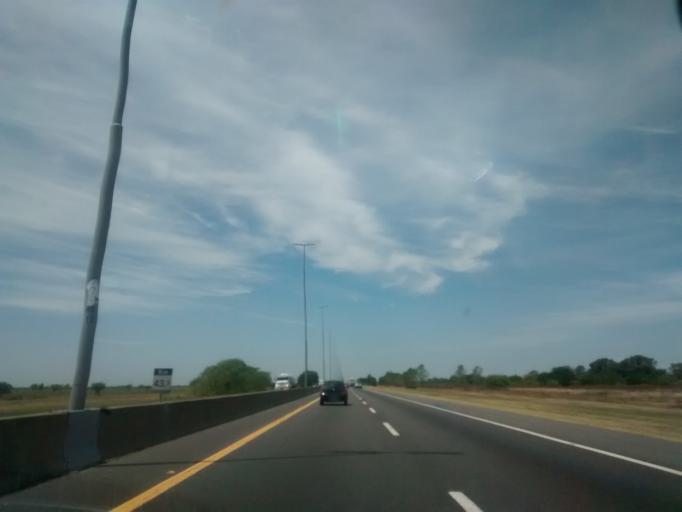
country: AR
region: Buenos Aires
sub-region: Partido de La Plata
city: La Plata
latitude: -34.8479
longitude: -58.0498
